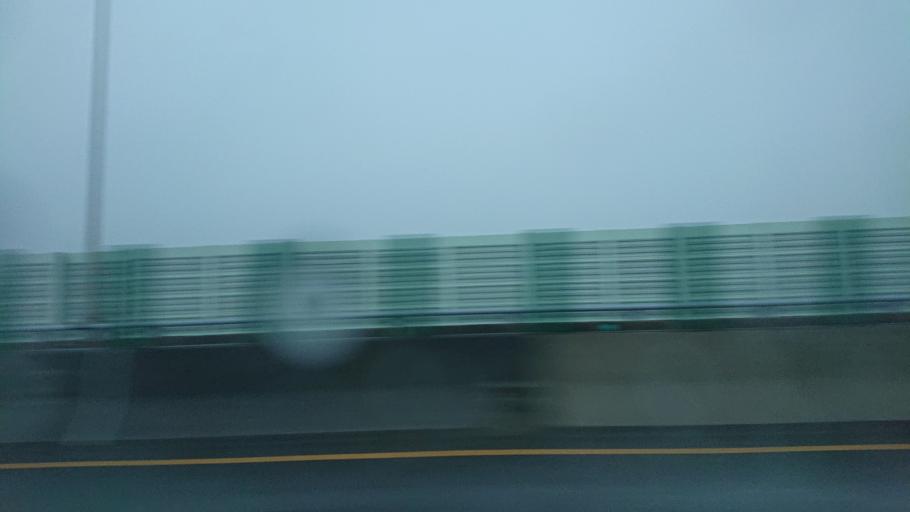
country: TW
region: Taiwan
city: Fengyuan
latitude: 24.3026
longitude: 120.5549
